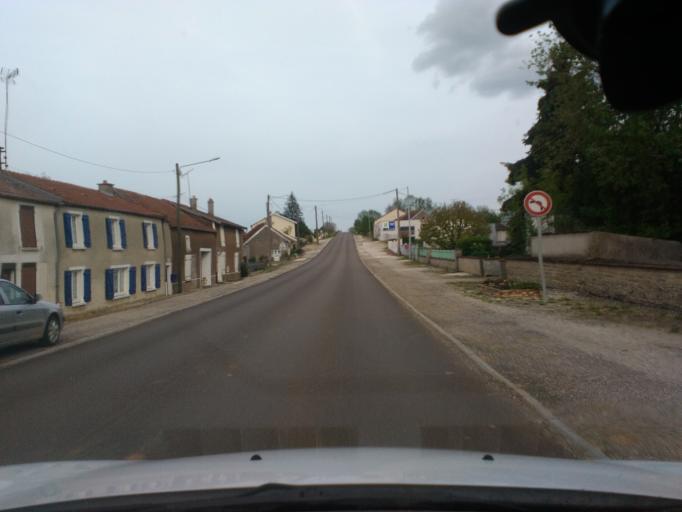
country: FR
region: Champagne-Ardenne
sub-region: Departement de la Haute-Marne
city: Chaumont
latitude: 48.1352
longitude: 5.0846
